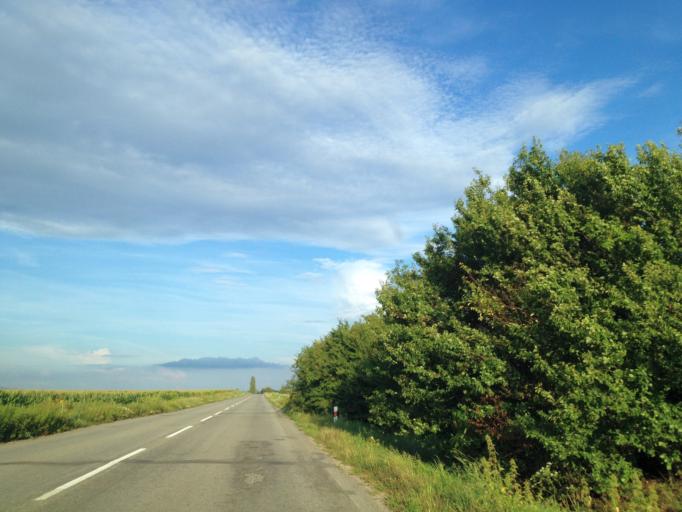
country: SK
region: Nitriansky
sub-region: Okres Komarno
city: Hurbanovo
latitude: 47.9054
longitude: 18.3370
